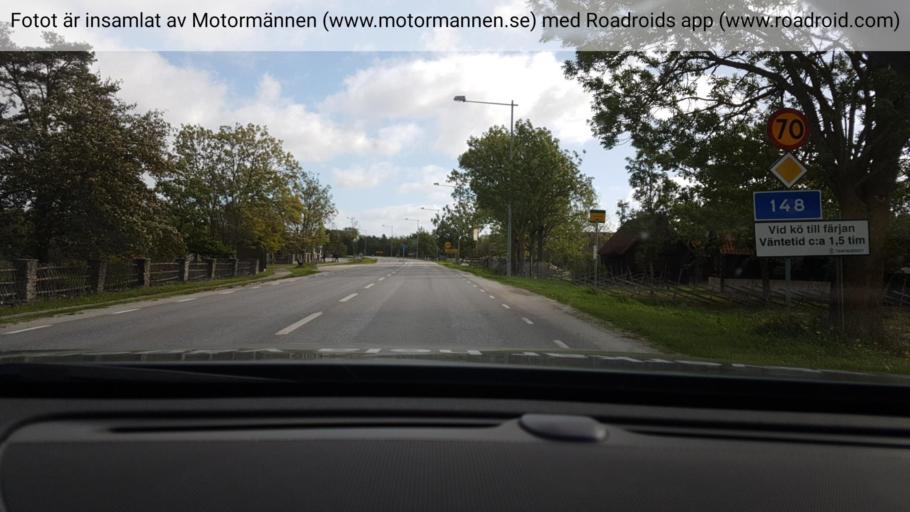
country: SE
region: Gotland
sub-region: Gotland
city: Slite
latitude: 57.8542
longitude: 19.0256
